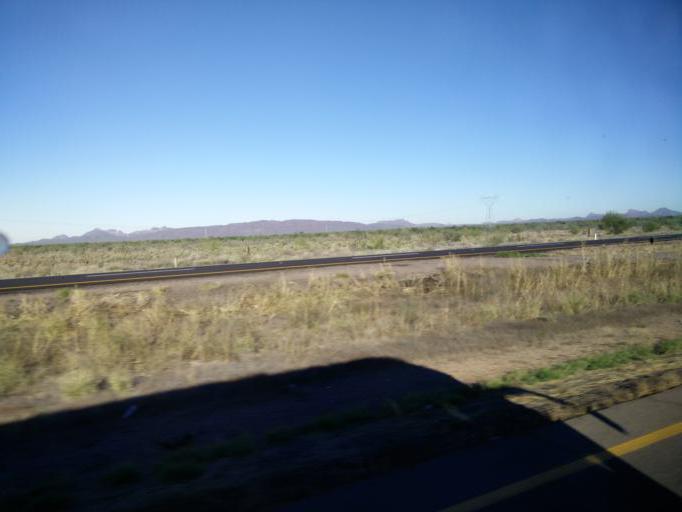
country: MX
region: Sonora
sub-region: Empalme
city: Empalme
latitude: 28.3099
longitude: -111.0417
